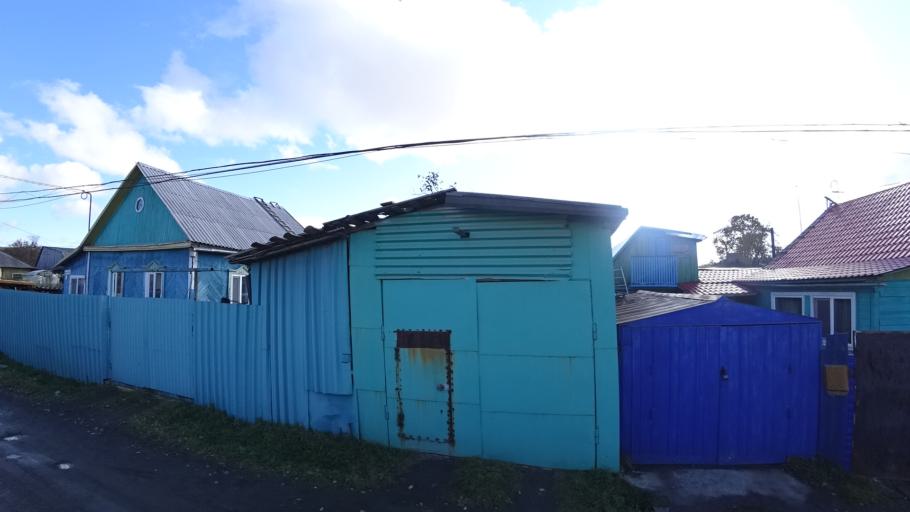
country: RU
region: Khabarovsk Krai
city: Amursk
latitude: 50.2335
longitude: 136.9186
